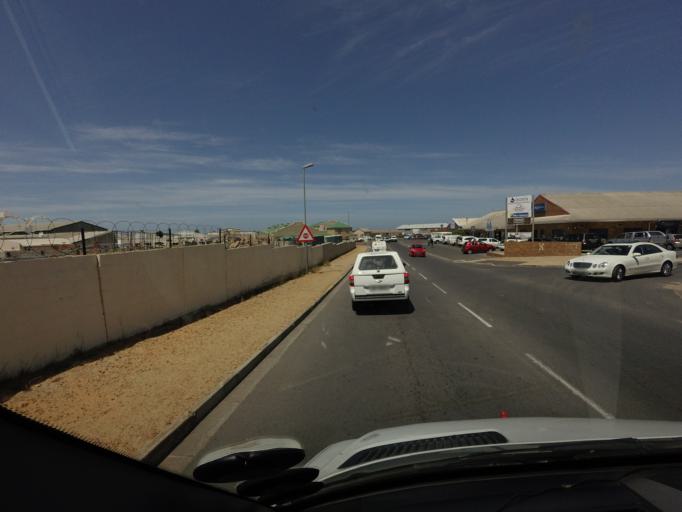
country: ZA
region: Western Cape
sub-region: Overberg District Municipality
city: Hermanus
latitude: -34.4201
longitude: 19.2249
